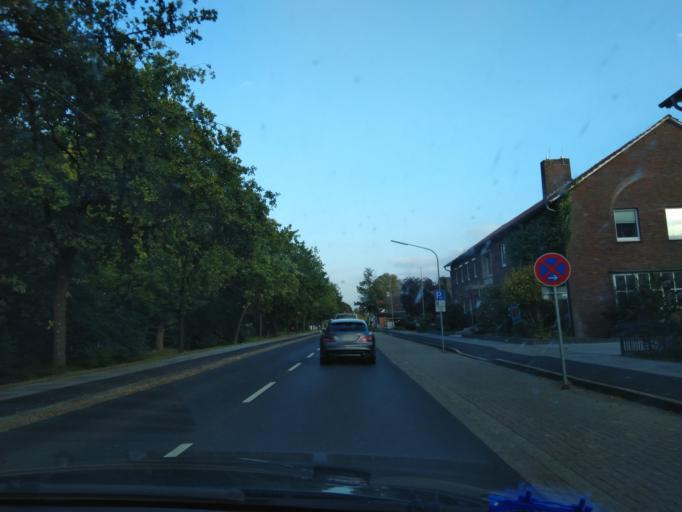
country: DE
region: Lower Saxony
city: Papenburg
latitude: 53.0757
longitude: 7.4078
